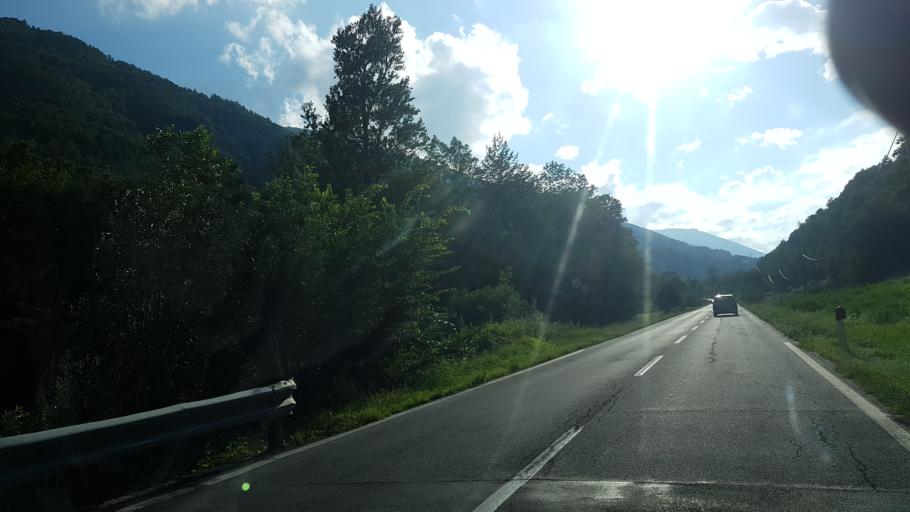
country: IT
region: Piedmont
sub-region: Provincia di Cuneo
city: Frassino
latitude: 44.5736
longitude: 7.2405
